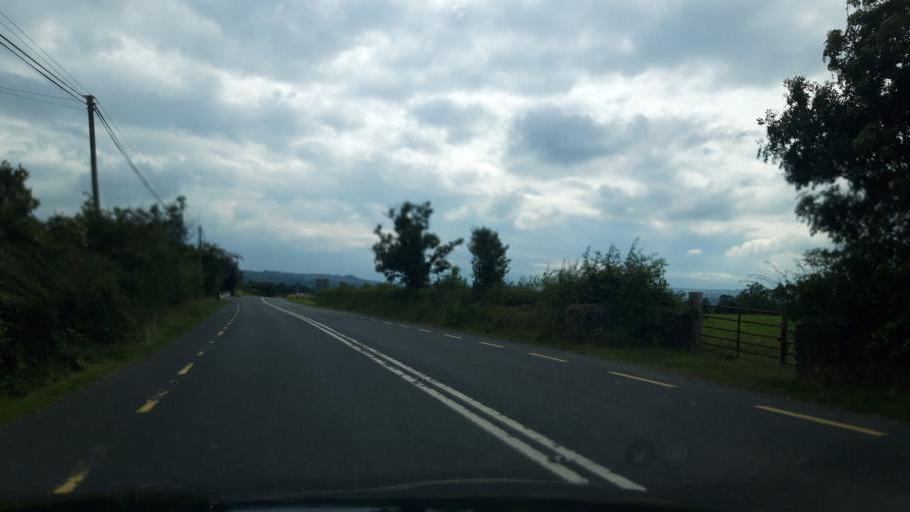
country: IE
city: Ballylinan
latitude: 52.8600
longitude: -7.1124
